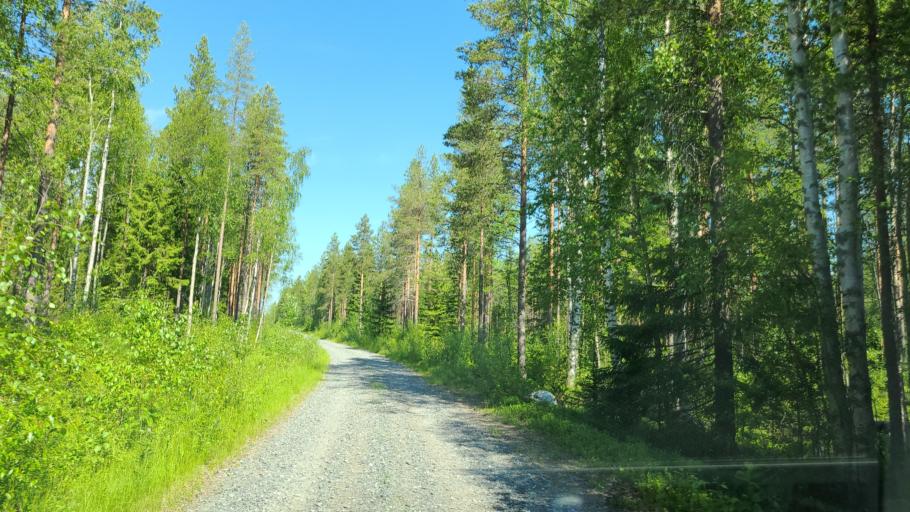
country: SE
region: Vaesterbotten
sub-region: Robertsfors Kommun
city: Robertsfors
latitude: 64.0944
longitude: 20.8351
